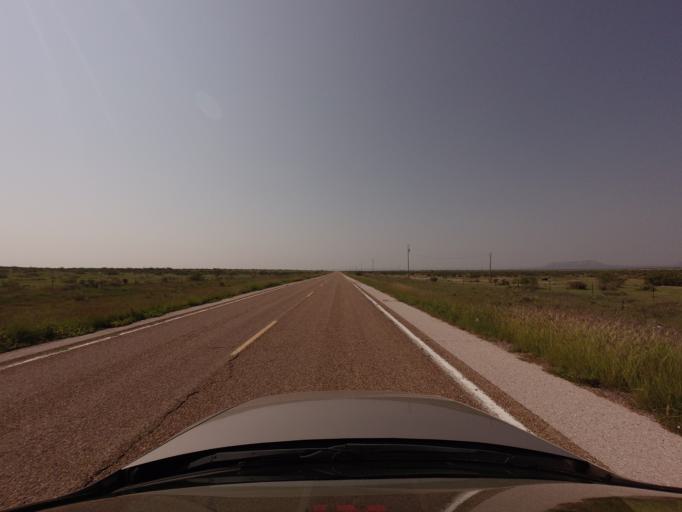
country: US
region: New Mexico
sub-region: Quay County
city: Tucumcari
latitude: 34.9951
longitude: -103.7455
